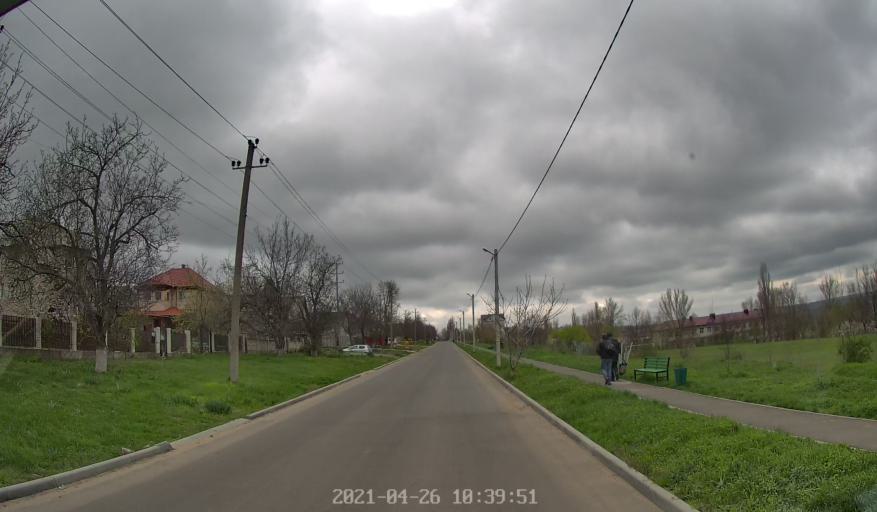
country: MD
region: Chisinau
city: Cricova
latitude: 47.1318
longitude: 28.8613
